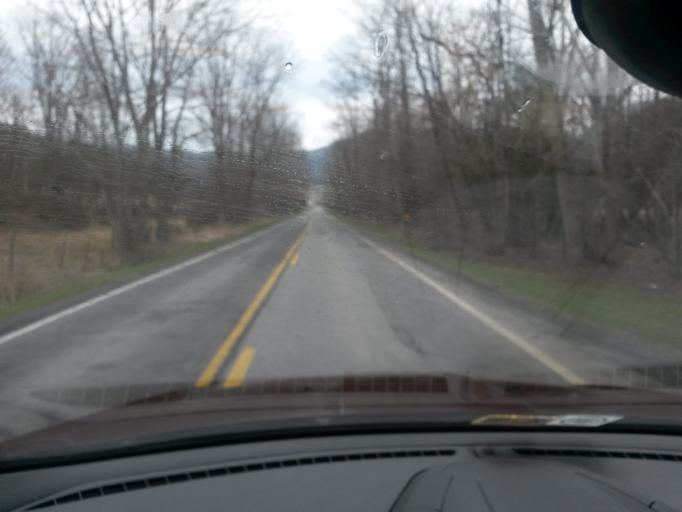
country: US
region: Virginia
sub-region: Highland County
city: Monterey
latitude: 38.3728
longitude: -79.6322
